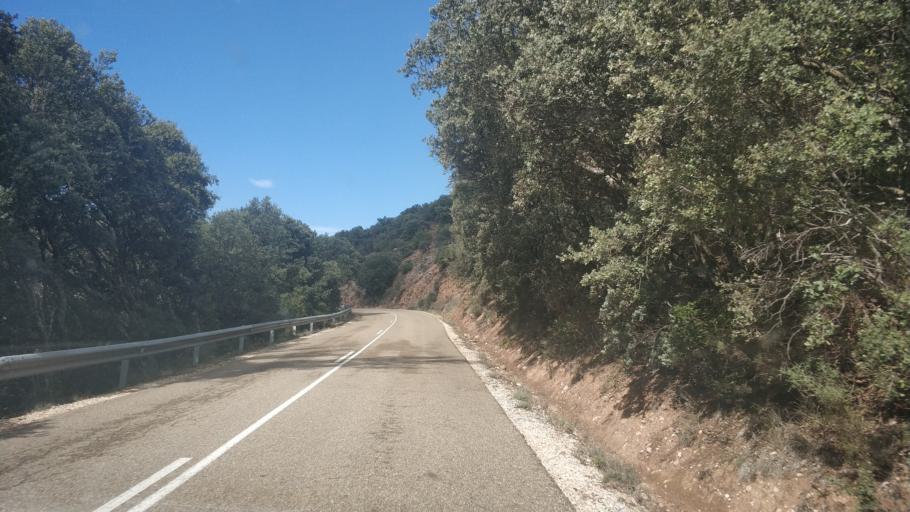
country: ES
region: Castille and Leon
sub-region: Provincia de Burgos
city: Retuerta
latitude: 42.0408
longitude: -3.4892
